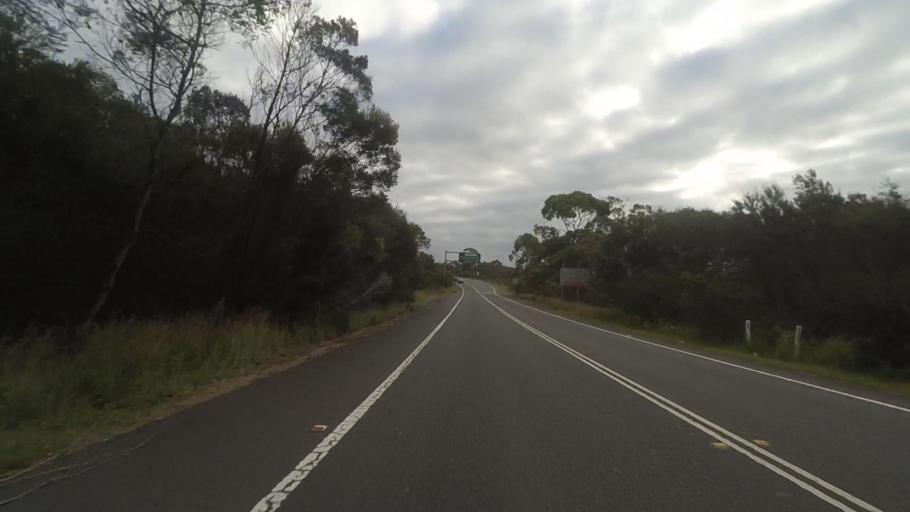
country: AU
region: New South Wales
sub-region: Sutherland Shire
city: Engadine
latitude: -34.0517
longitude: 150.9735
